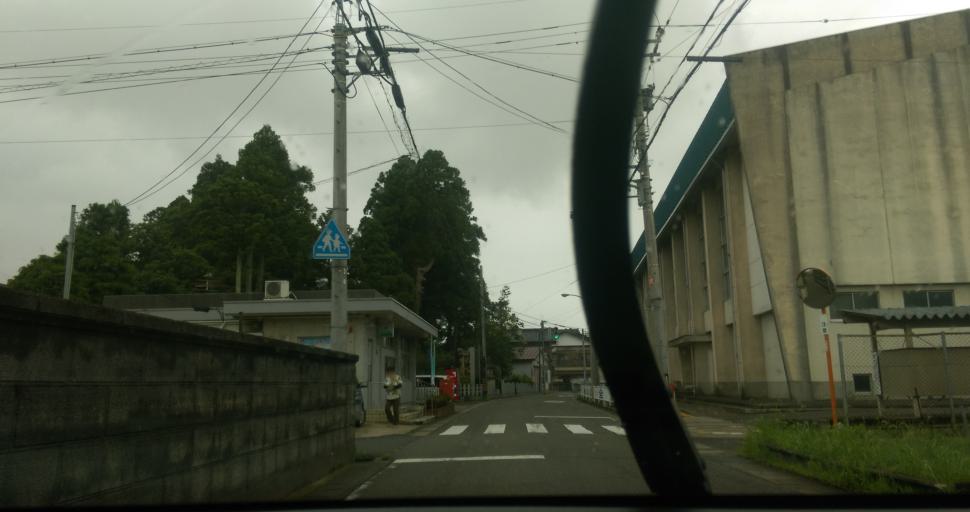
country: JP
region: Fukui
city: Fukui-shi
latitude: 36.0253
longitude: 136.2329
